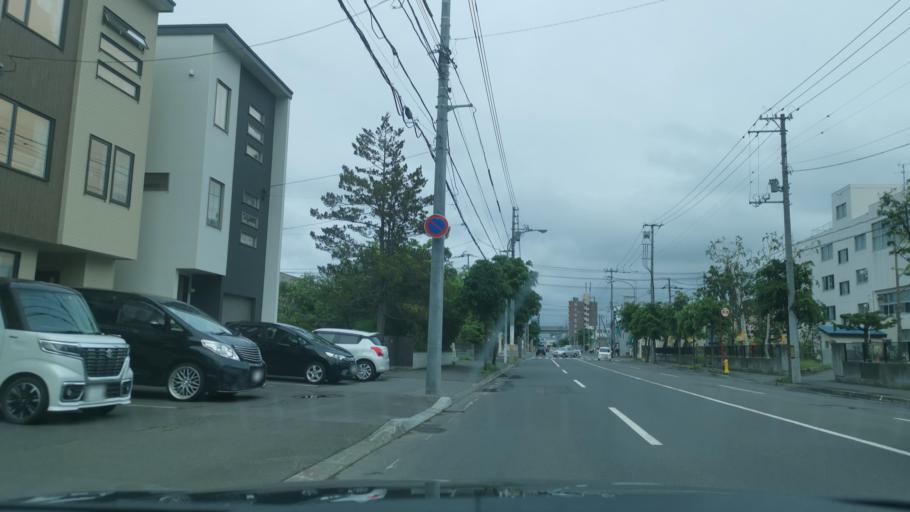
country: JP
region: Hokkaido
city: Sapporo
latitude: 43.1050
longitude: 141.3228
